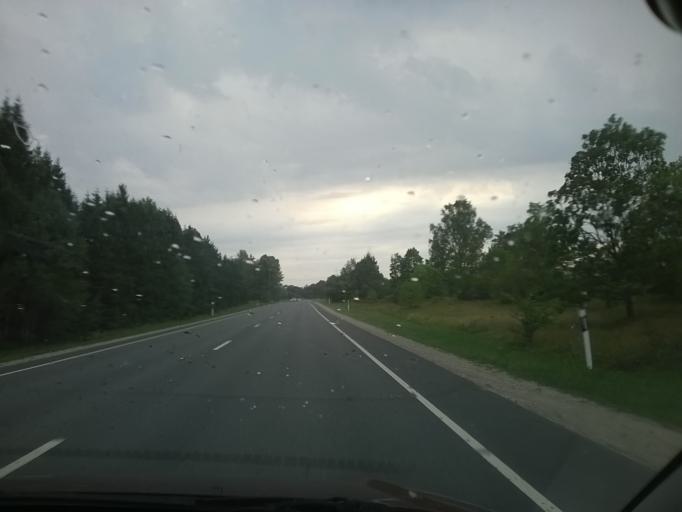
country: EE
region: Harju
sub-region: Nissi vald
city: Turba
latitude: 59.0453
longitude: 24.1723
